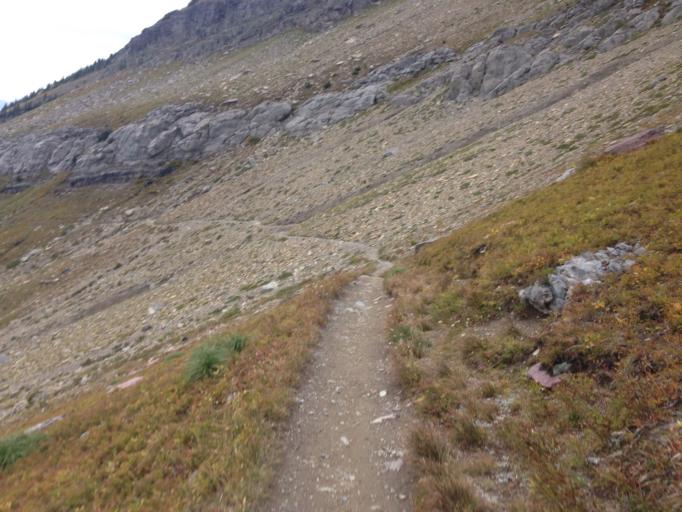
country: US
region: Montana
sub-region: Flathead County
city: Columbia Falls
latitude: 48.7435
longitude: -113.7332
